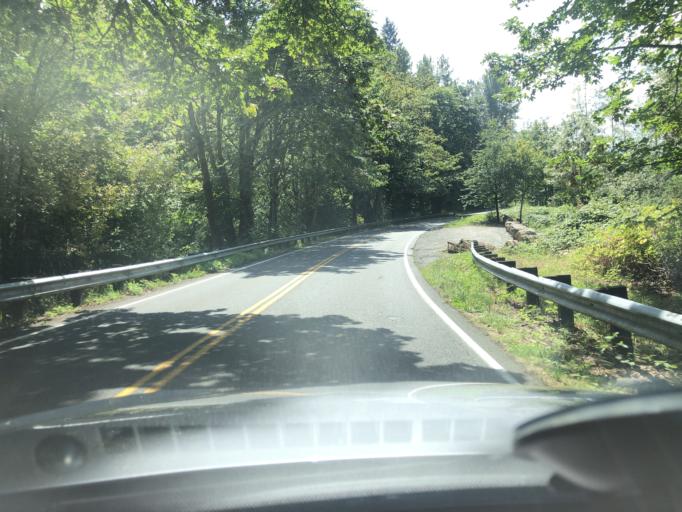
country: US
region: Washington
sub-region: King County
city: Lea Hill
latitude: 47.3436
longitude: -122.2051
